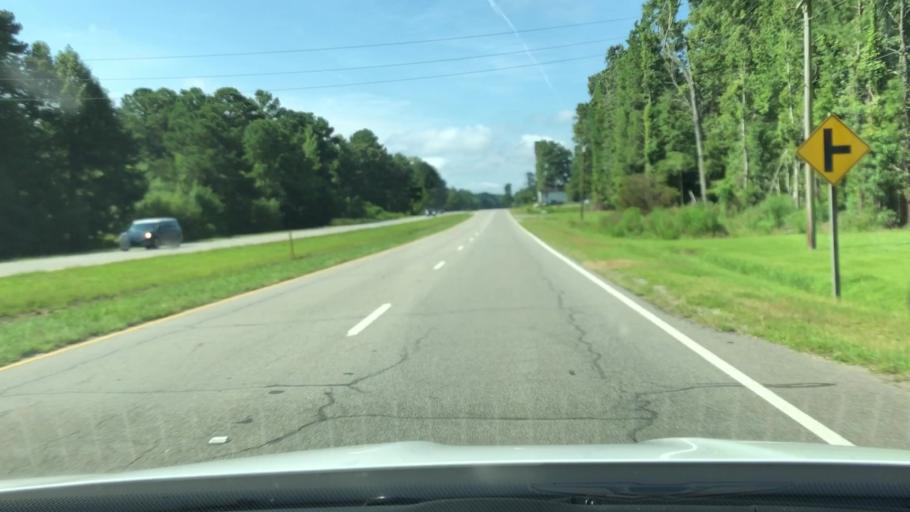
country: US
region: North Carolina
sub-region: Bertie County
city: Windsor
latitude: 35.9542
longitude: -76.9550
